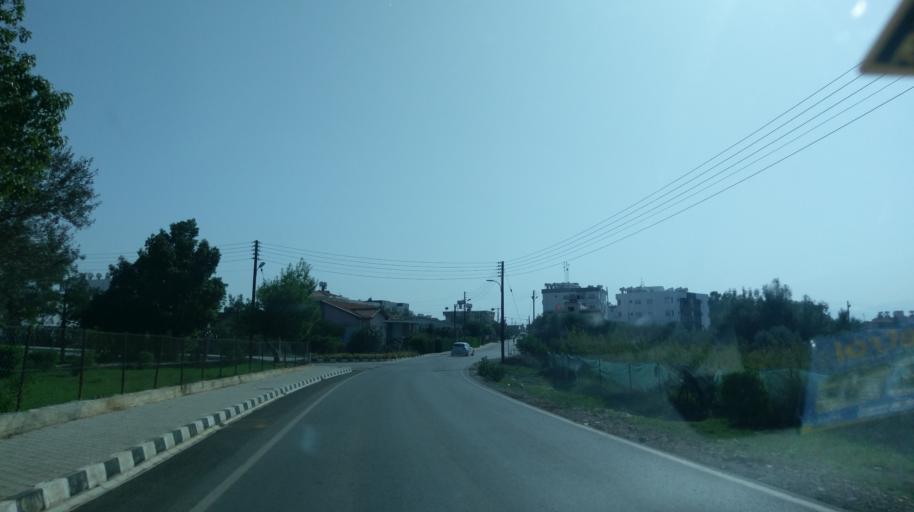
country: CY
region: Lefkosia
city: Morfou
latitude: 35.2487
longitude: 33.0376
